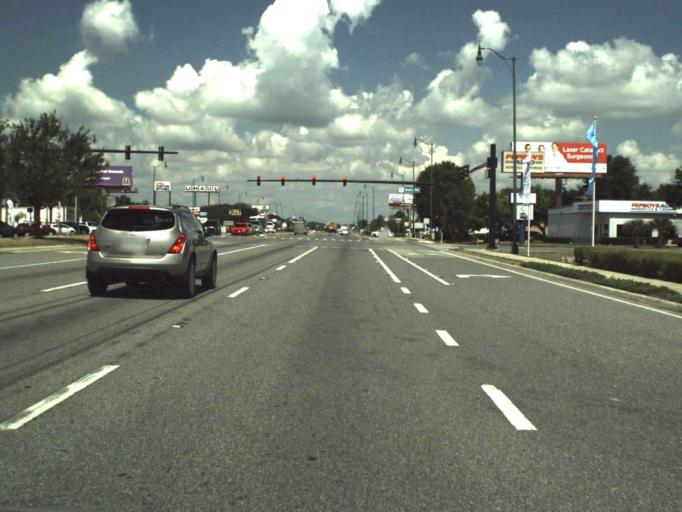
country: US
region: Florida
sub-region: Lake County
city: Silver Lake
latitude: 28.8231
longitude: -81.7863
